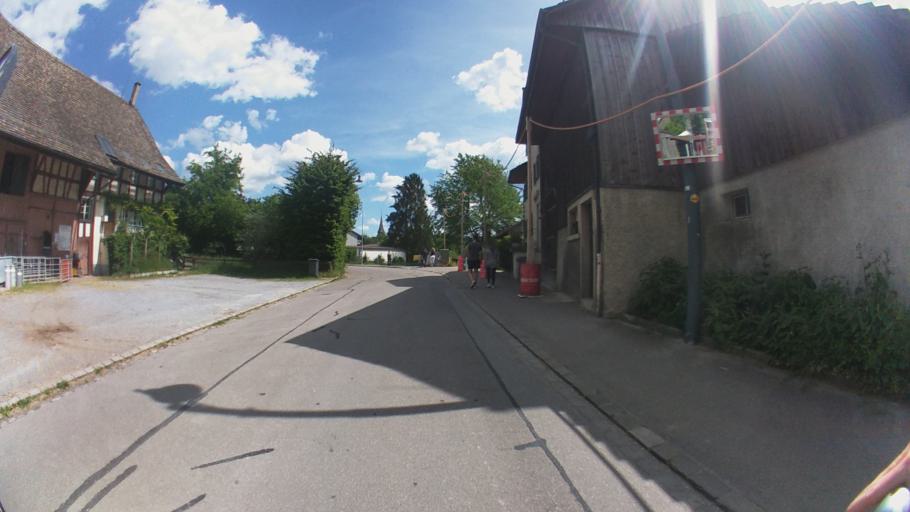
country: CH
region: Zurich
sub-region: Bezirk Zuerich
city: Zuerich (Kreis 11) / Affoltern
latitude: 47.4264
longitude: 8.5070
